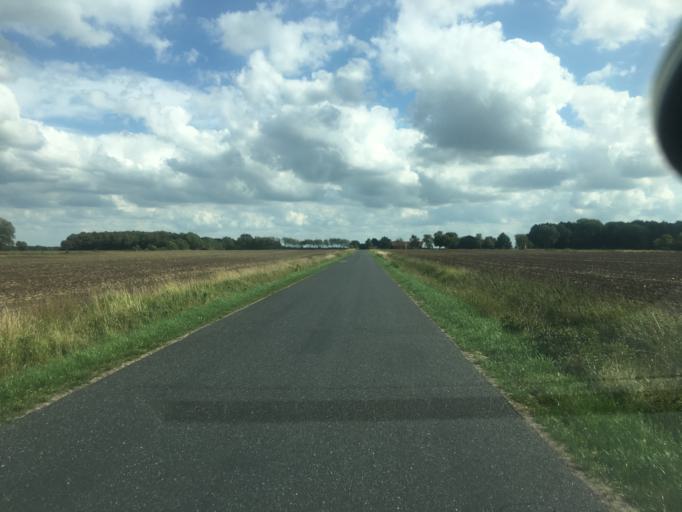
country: DK
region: South Denmark
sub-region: Tonder Kommune
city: Logumkloster
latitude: 55.0182
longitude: 8.9929
